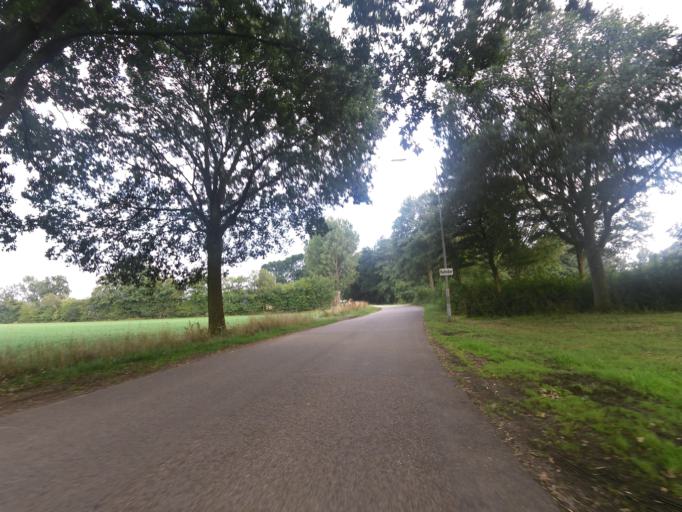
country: NL
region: Gelderland
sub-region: Oude IJsselstreek
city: Gendringen
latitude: 51.9116
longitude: 6.3275
